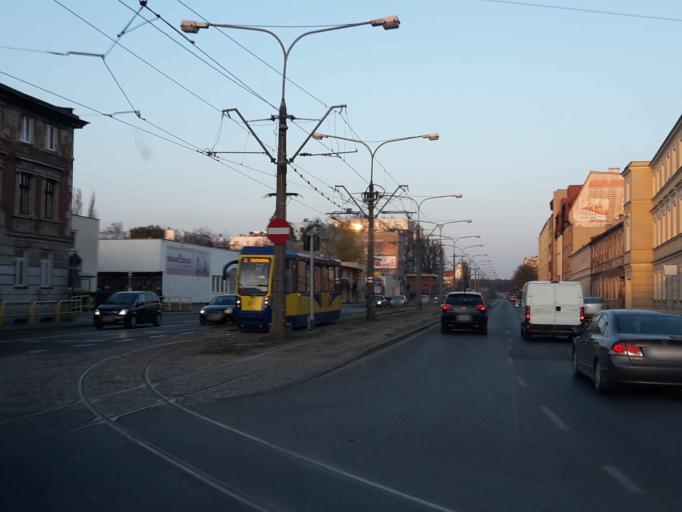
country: PL
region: Kujawsko-Pomorskie
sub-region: Torun
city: Torun
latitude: 53.0137
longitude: 18.5716
